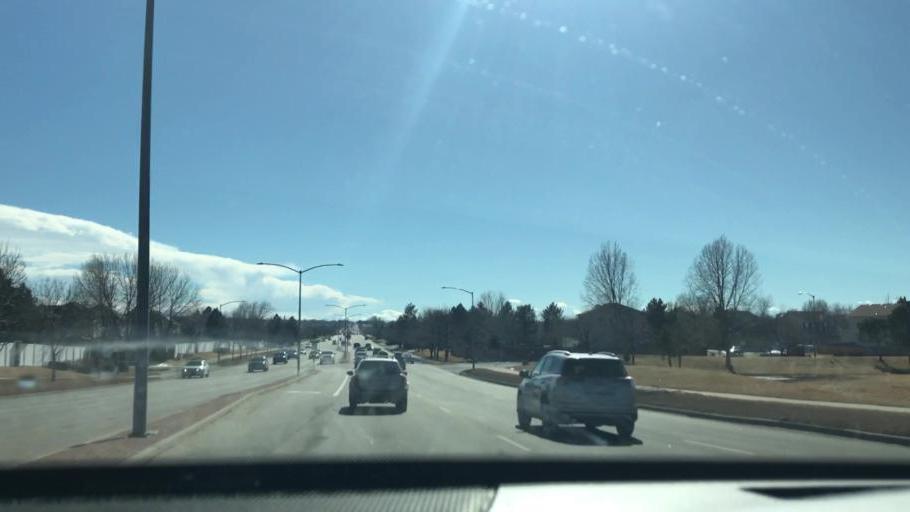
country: US
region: Colorado
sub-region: Broomfield County
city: Broomfield
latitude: 39.9098
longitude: -105.0530
